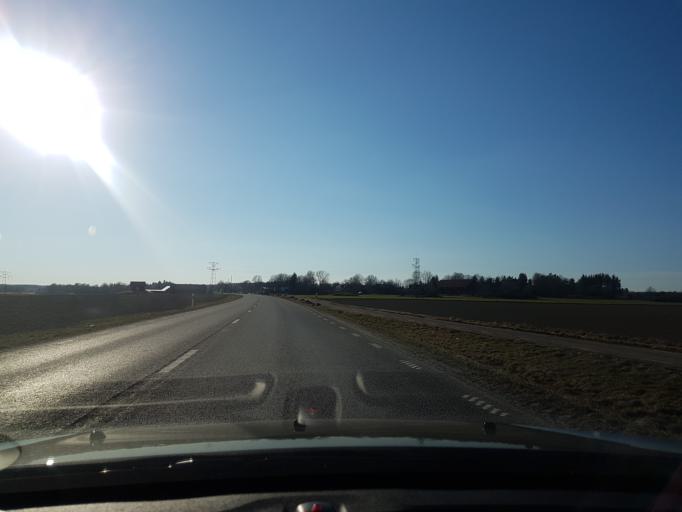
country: SE
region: Uppsala
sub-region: Uppsala Kommun
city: Uppsala
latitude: 59.8482
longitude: 17.5402
